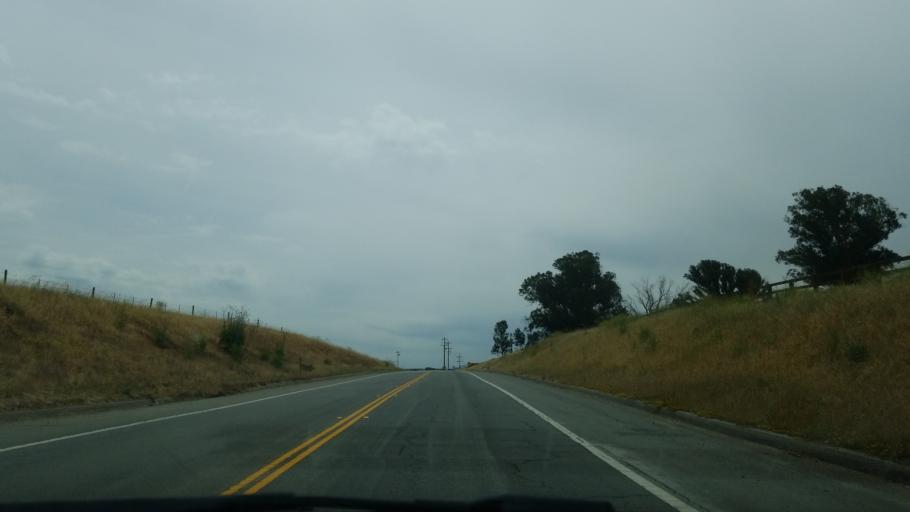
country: US
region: California
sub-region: San Luis Obispo County
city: San Luis Obispo
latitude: 35.2495
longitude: -120.6200
